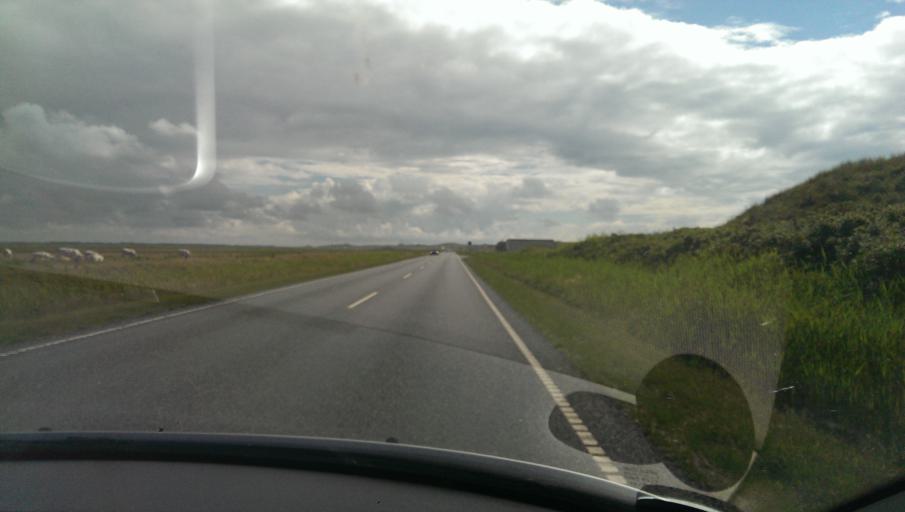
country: DK
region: Central Jutland
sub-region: Ringkobing-Skjern Kommune
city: Ringkobing
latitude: 56.1979
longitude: 8.1304
